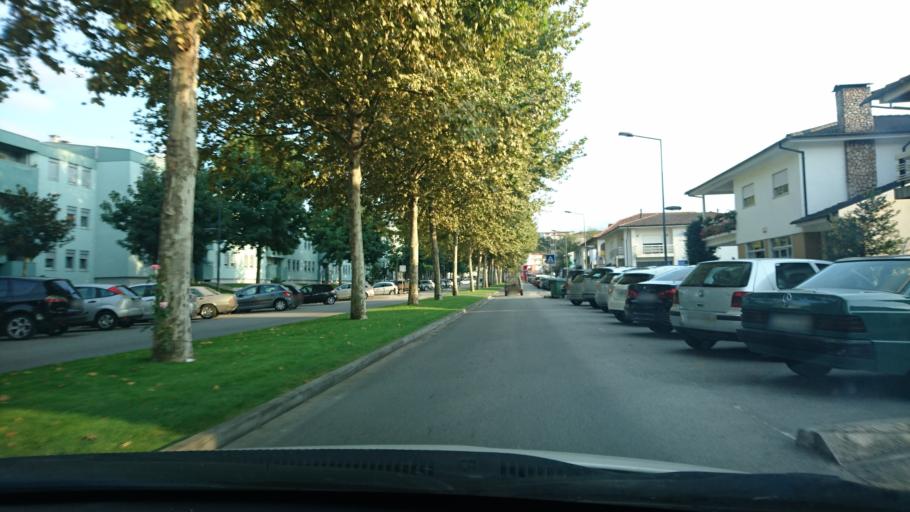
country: PT
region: Vila Real
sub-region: Mondim de Basto
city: Mondim de Basto
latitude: 41.4115
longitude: -7.9555
